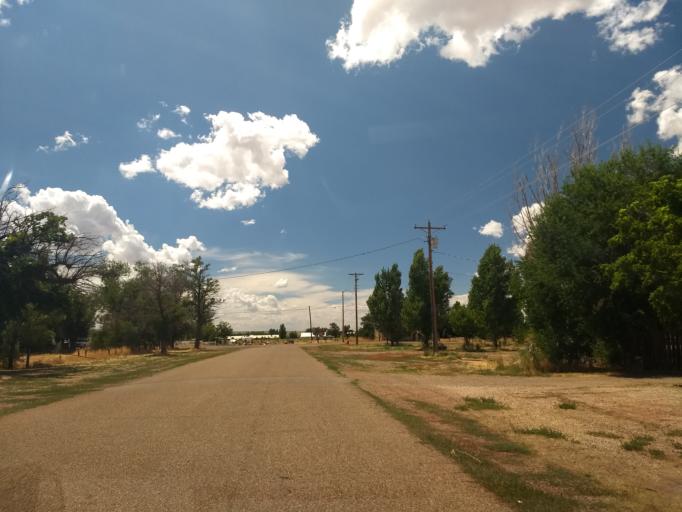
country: US
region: Arizona
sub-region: Coconino County
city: Fredonia
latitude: 36.9464
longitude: -112.5244
